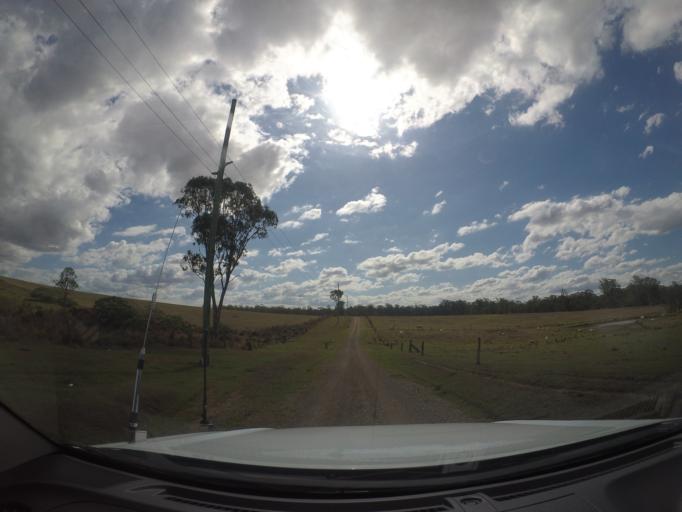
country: AU
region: Queensland
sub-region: Logan
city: North Maclean
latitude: -27.8083
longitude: 153.0008
